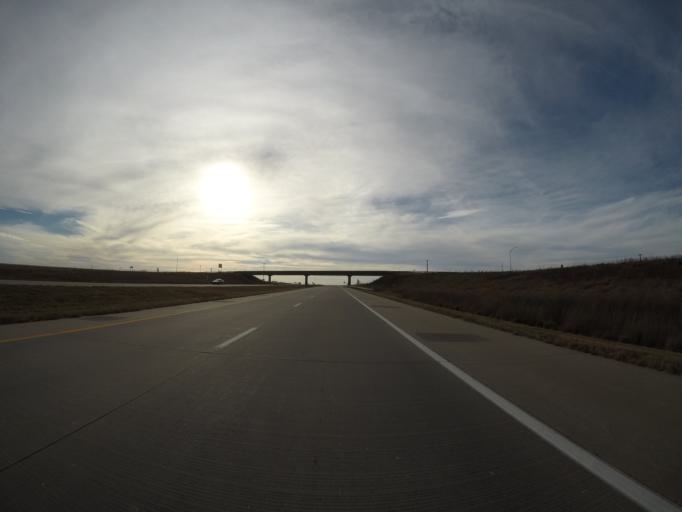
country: US
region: Kansas
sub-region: Franklin County
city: Wellsville
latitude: 38.6710
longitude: -95.1544
